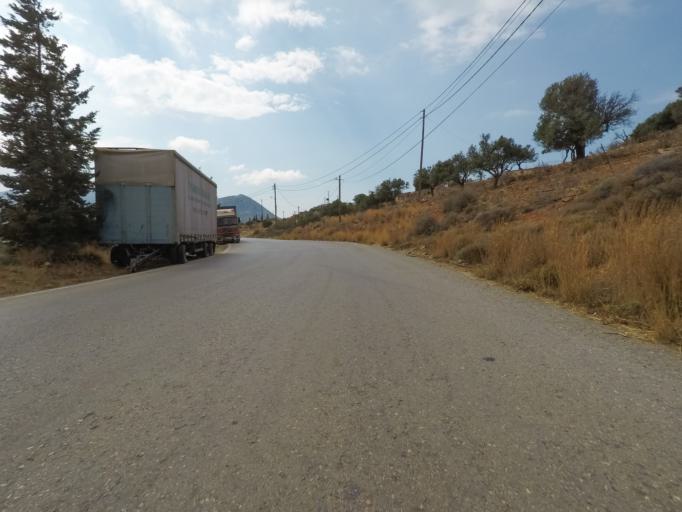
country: GR
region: Crete
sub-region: Nomos Lasithiou
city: Neapoli
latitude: 35.2618
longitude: 25.6096
